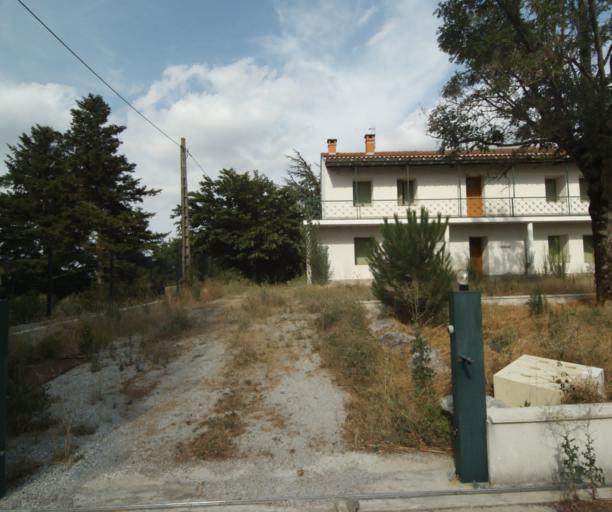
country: FR
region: Midi-Pyrenees
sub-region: Departement de la Haute-Garonne
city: Revel
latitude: 43.4437
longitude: 2.0291
